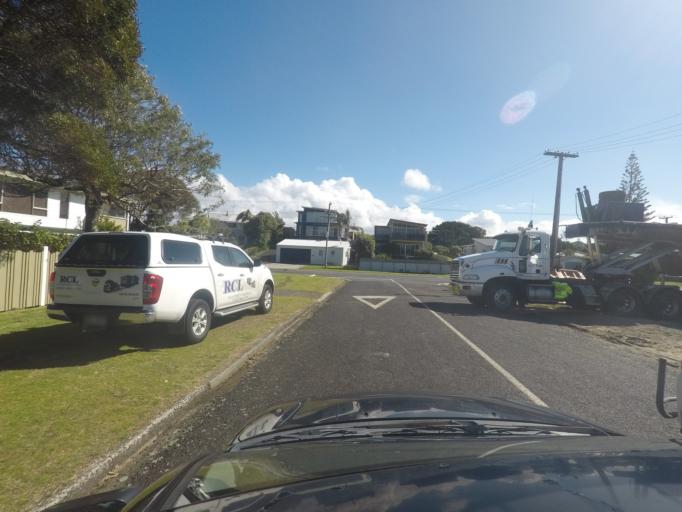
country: NZ
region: Bay of Plenty
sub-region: Western Bay of Plenty District
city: Waihi Beach
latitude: -37.4190
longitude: 175.9506
